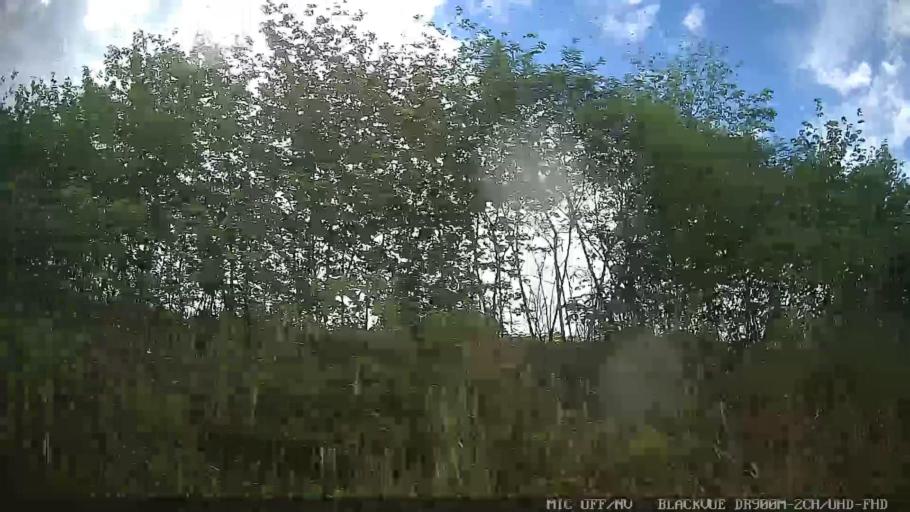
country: BR
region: Sao Paulo
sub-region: Jaguariuna
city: Jaguariuna
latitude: -22.6637
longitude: -47.0548
